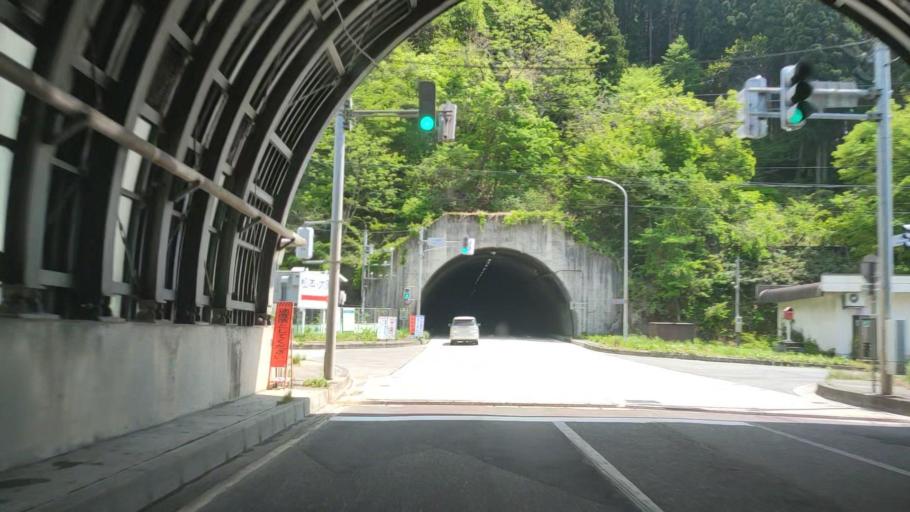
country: JP
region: Nagano
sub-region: Kitaazumi Gun
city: Hakuba
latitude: 36.8131
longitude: 137.9109
